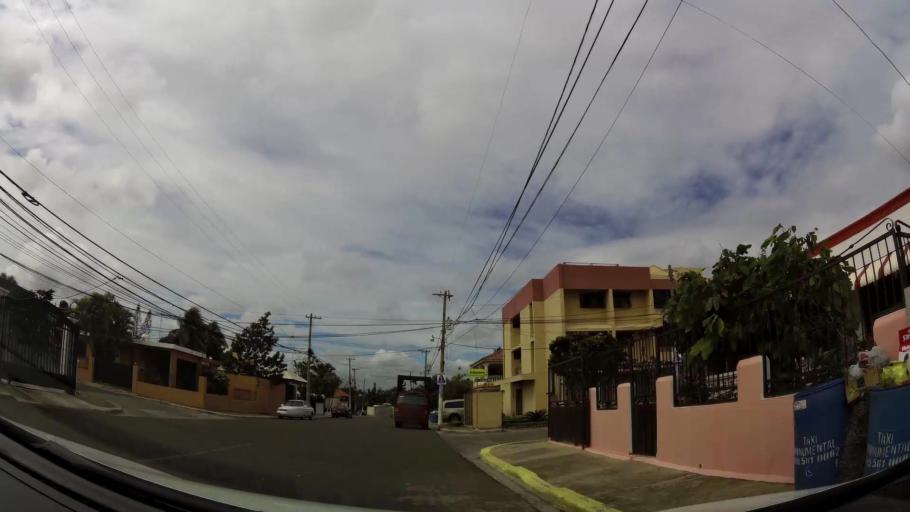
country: DO
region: Santiago
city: Santiago de los Caballeros
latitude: 19.4417
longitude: -70.6740
